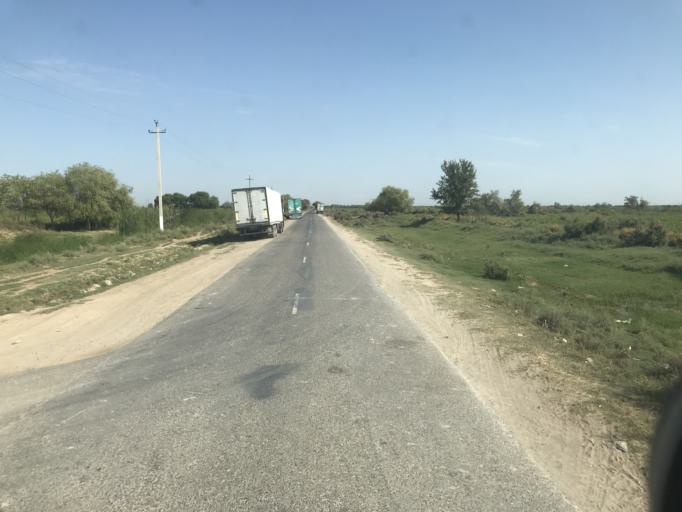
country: KZ
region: Ongtustik Qazaqstan
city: Myrzakent
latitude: 40.6674
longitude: 68.6332
